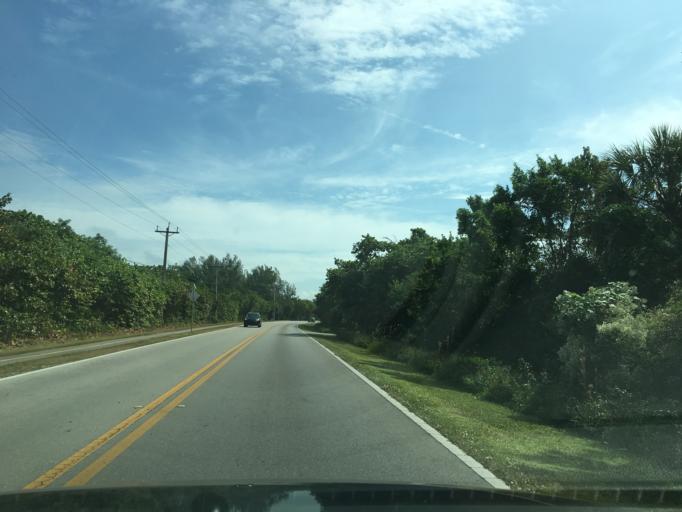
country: US
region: Florida
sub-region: Lee County
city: Saint James City
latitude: 26.4701
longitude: -82.1588
